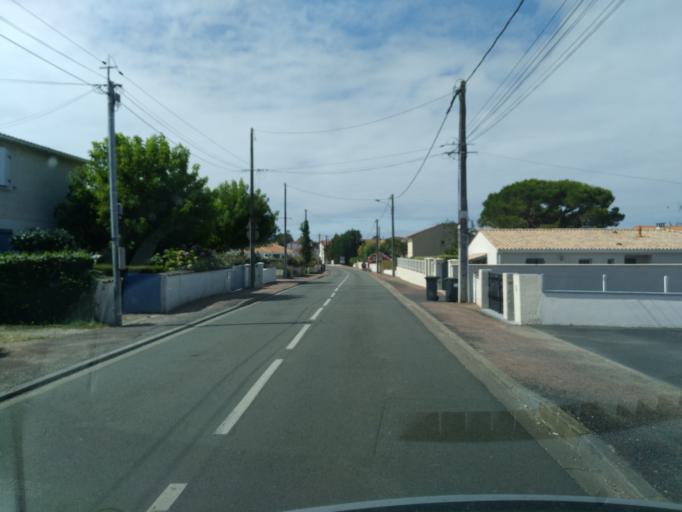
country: FR
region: Poitou-Charentes
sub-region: Departement de la Charente-Maritime
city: Saint-Palais-sur-Mer
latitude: 45.6588
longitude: -1.0757
